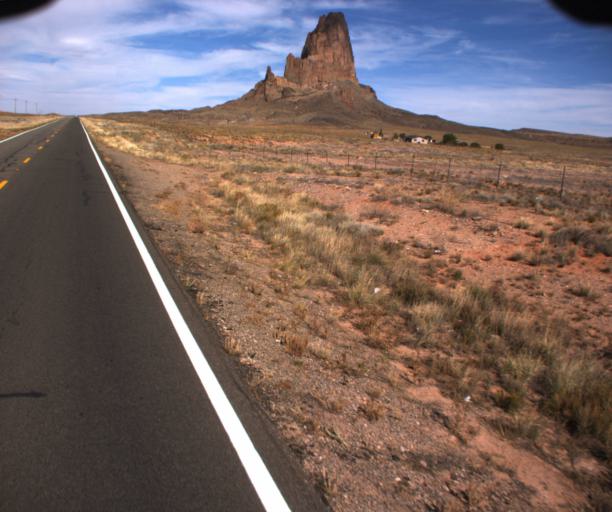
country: US
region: Arizona
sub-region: Navajo County
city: Kayenta
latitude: 36.8062
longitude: -110.2329
